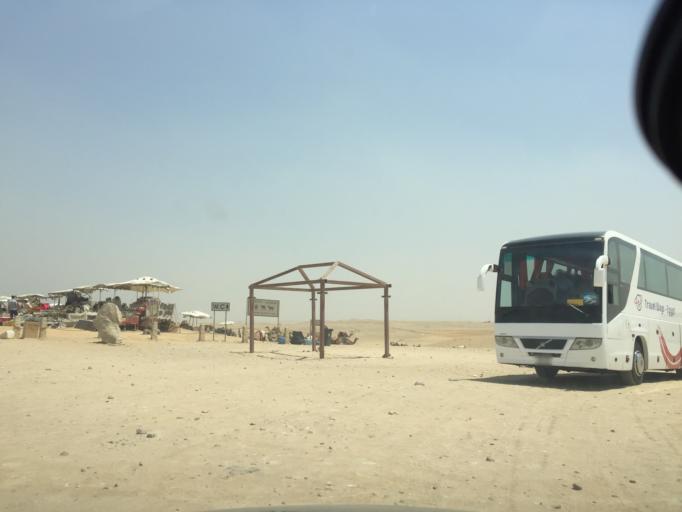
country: EG
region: Al Jizah
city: Al Jizah
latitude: 29.9726
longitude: 31.1200
